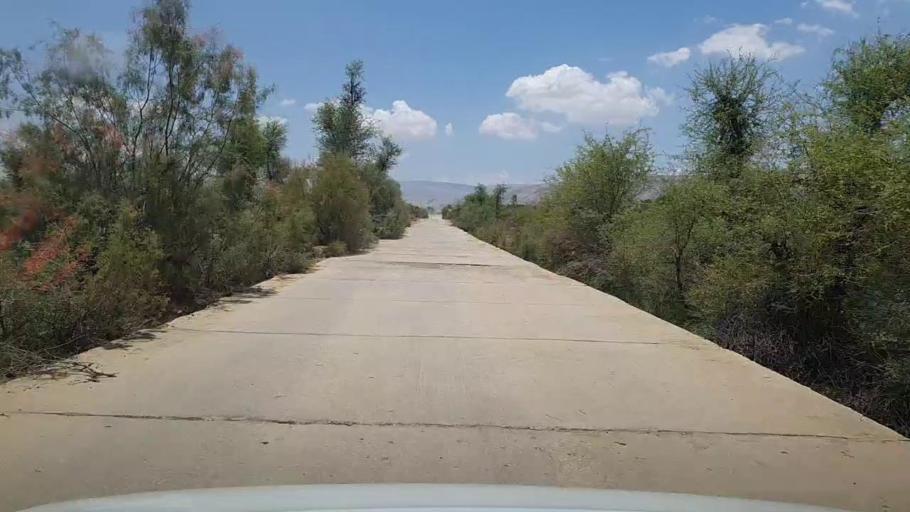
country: PK
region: Sindh
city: Bhan
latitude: 26.2787
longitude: 67.5281
